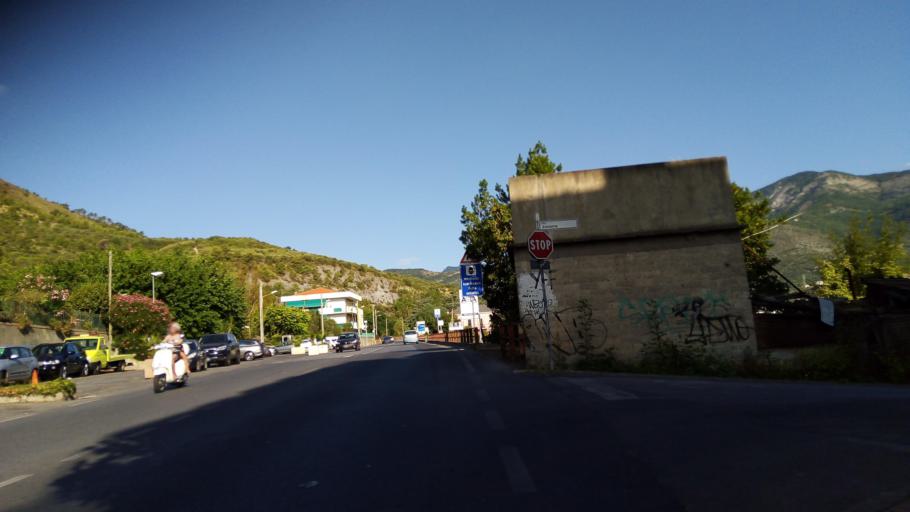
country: IT
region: Liguria
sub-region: Provincia di Savona
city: Borghetto Santo Spirito
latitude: 44.1137
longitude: 8.2329
